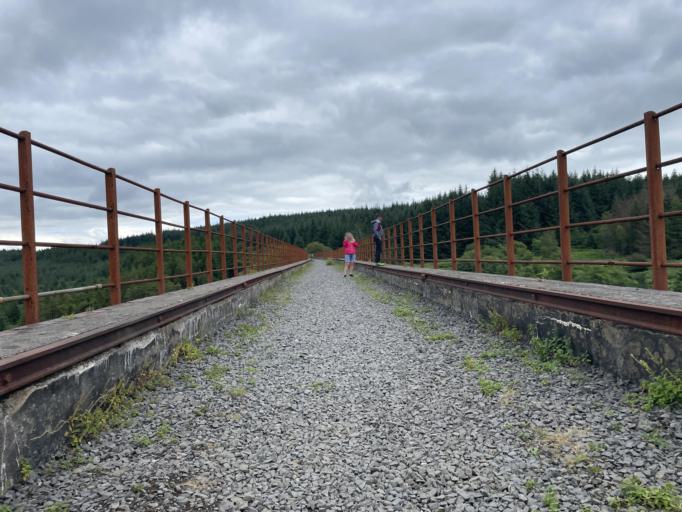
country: GB
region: Scotland
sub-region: Dumfries and Galloway
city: Newton Stewart
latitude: 54.9527
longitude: -4.2521
